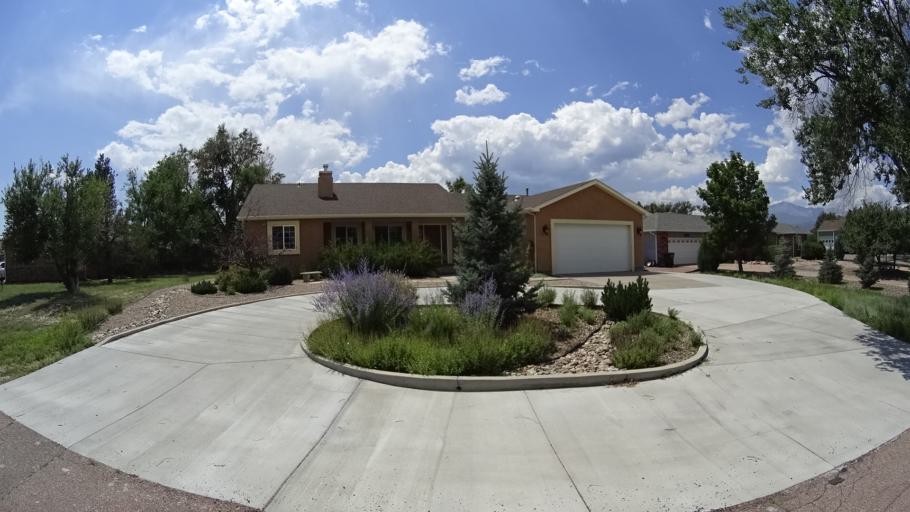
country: US
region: Colorado
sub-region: El Paso County
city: Air Force Academy
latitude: 38.9410
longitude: -104.8058
